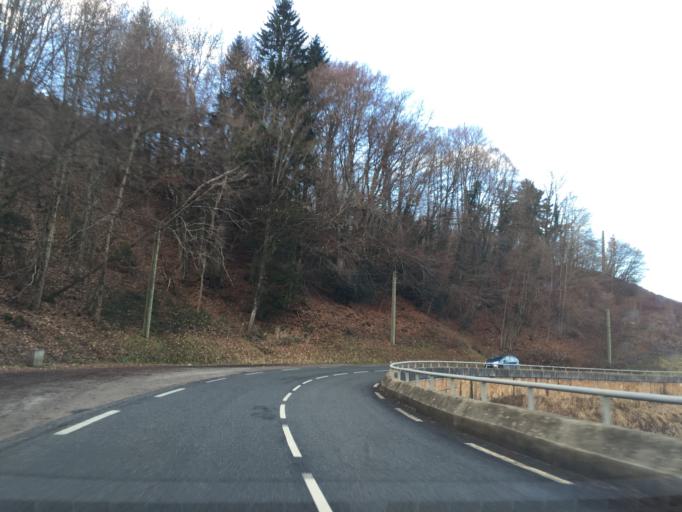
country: FR
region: Rhone-Alpes
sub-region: Departement de la Haute-Savoie
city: Gruffy
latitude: 45.7593
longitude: 6.0565
